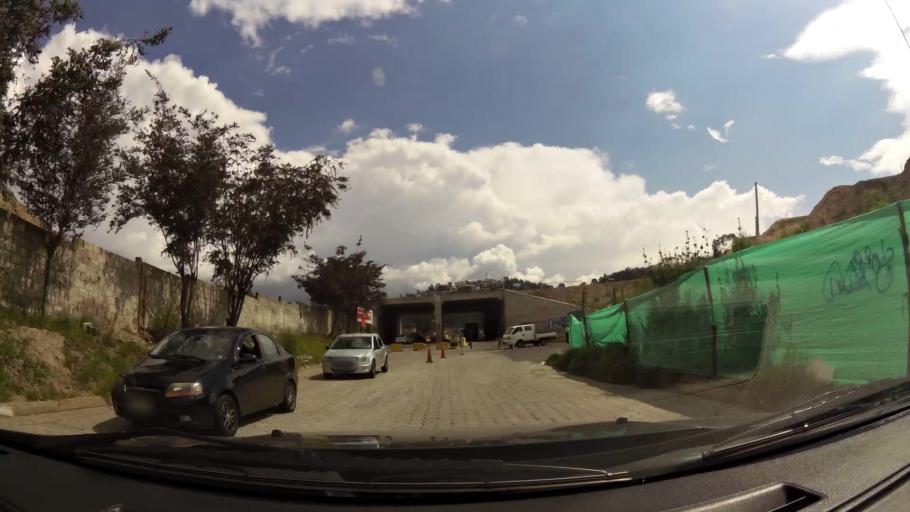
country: EC
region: Pichincha
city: Quito
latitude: -0.1069
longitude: -78.4587
